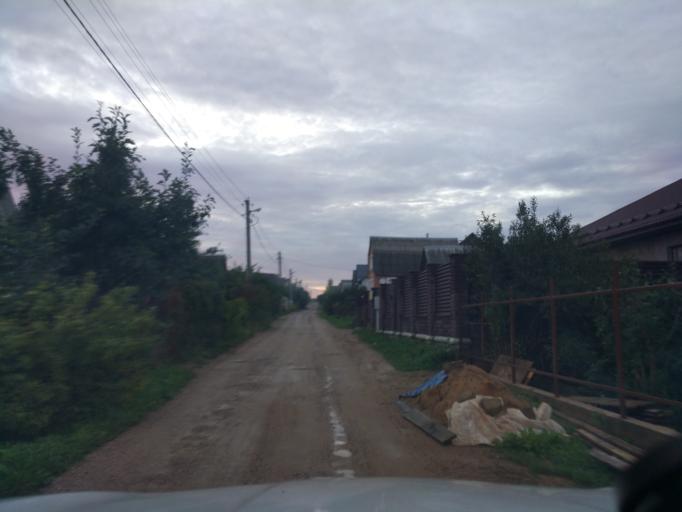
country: BY
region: Minsk
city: Astrashytski Haradok
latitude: 54.0871
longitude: 27.6995
